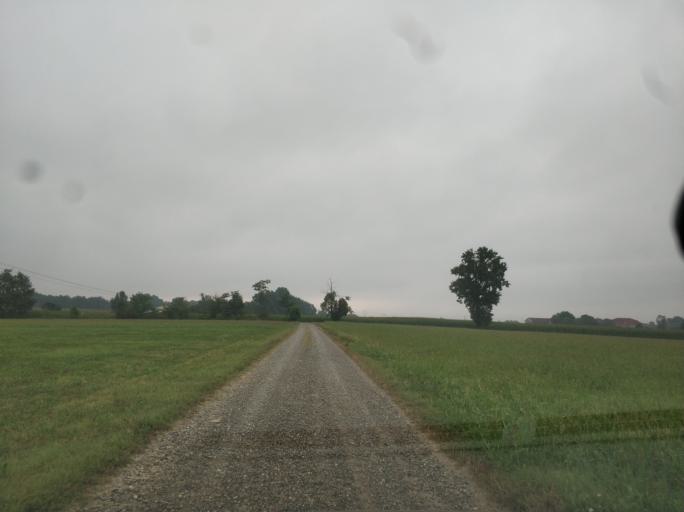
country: IT
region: Piedmont
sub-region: Provincia di Torino
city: Rivarossa
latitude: 45.2251
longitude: 7.6958
